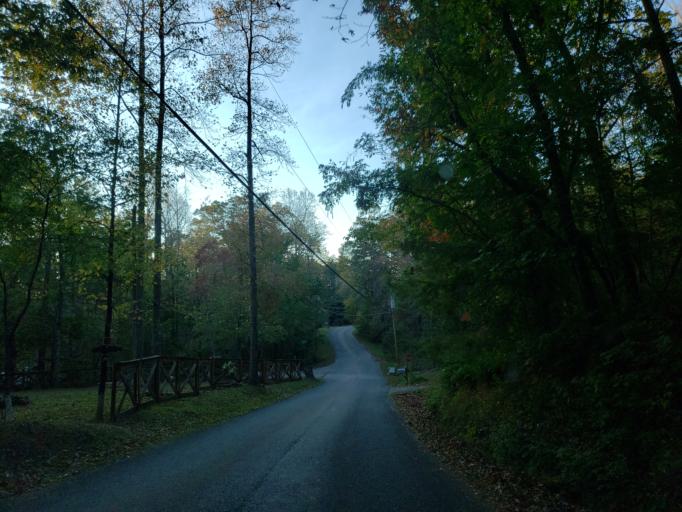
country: US
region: Georgia
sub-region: Gilmer County
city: Ellijay
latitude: 34.6492
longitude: -84.2867
